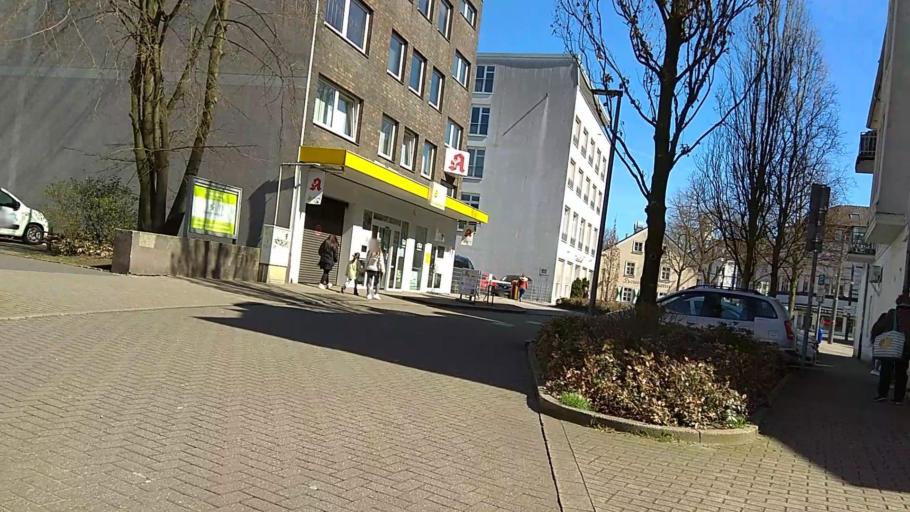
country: DE
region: North Rhine-Westphalia
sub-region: Regierungsbezirk Munster
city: Gladbeck
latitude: 51.5768
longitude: 7.0507
